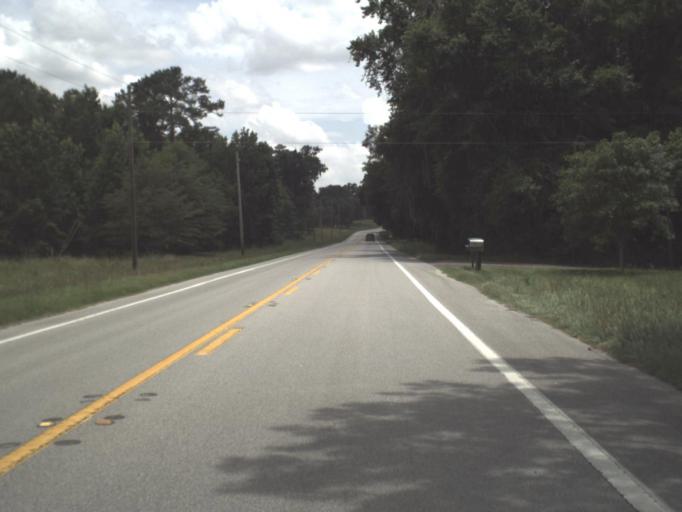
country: US
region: Florida
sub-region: Madison County
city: Madison
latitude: 30.5178
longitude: -83.4226
